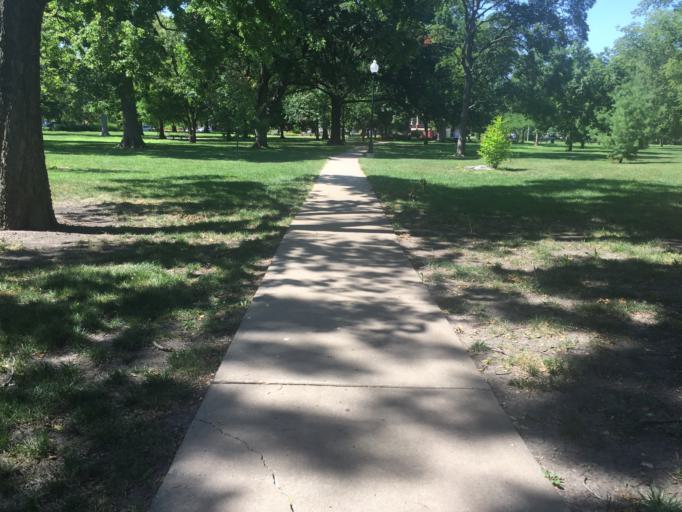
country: US
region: Kansas
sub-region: Douglas County
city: Lawrence
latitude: 38.9608
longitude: -95.2346
